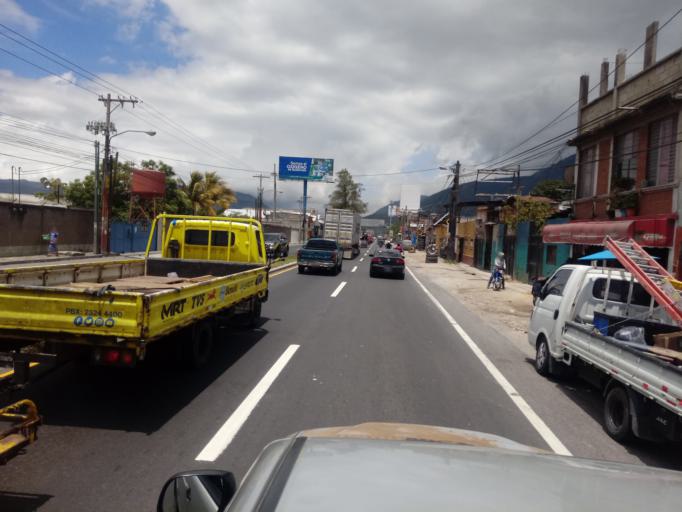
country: GT
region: Guatemala
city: Amatitlan
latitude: 14.4813
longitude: -90.6300
